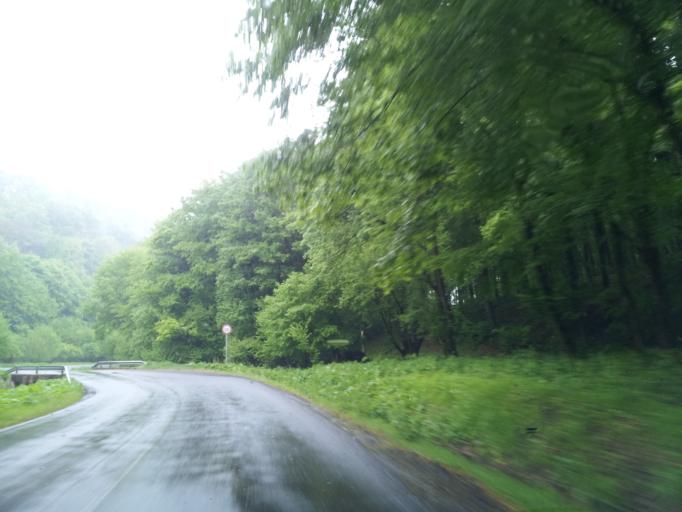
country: HU
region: Baranya
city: Komlo
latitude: 46.2139
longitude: 18.3005
